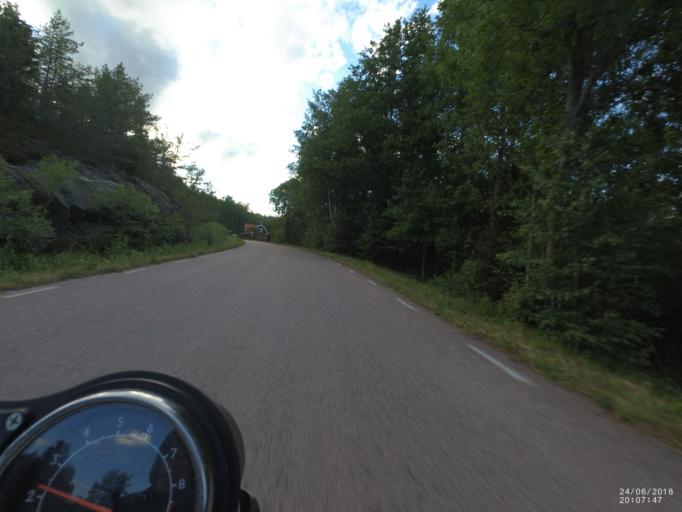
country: SE
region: Soedermanland
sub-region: Nykopings Kommun
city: Nykoping
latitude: 58.8188
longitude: 17.1397
